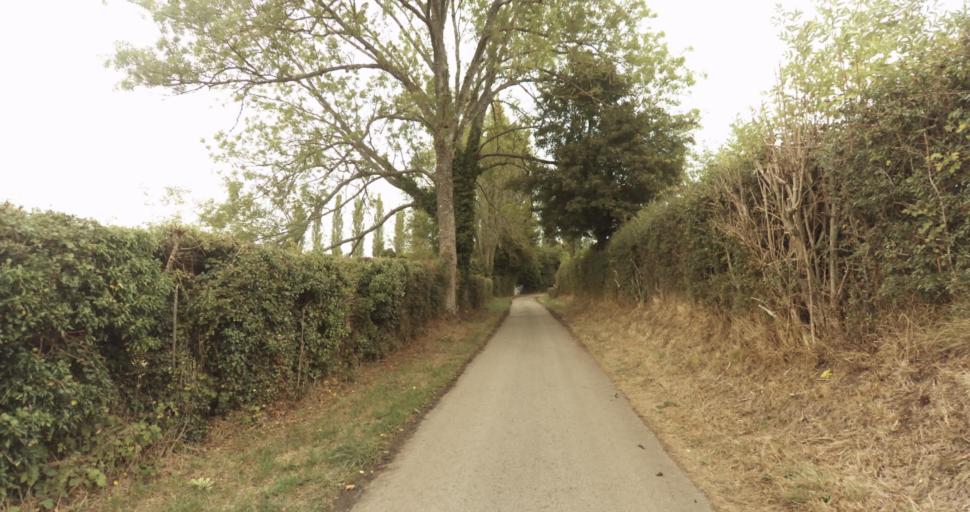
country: FR
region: Lower Normandy
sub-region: Departement de l'Orne
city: Gace
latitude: 48.8268
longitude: 0.2821
